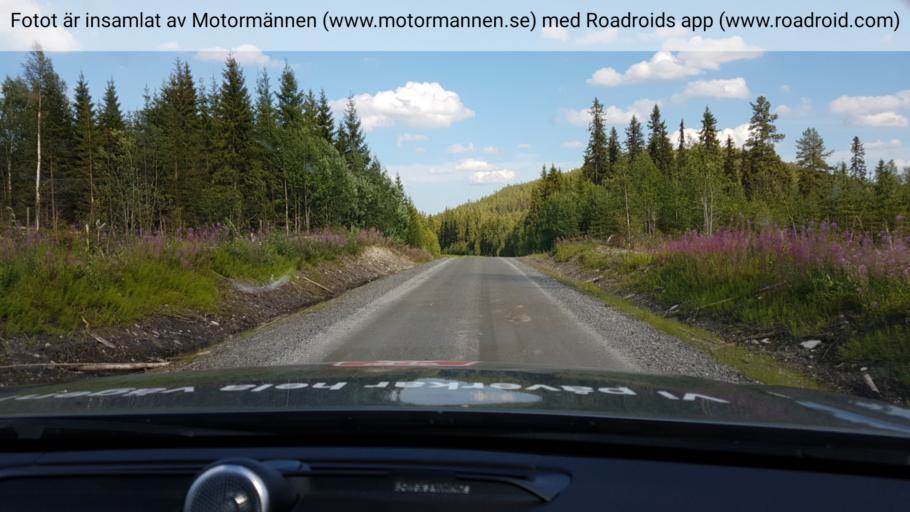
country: SE
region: Vaesterbotten
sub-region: Dorotea Kommun
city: Dorotea
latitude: 63.9192
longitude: 16.2131
